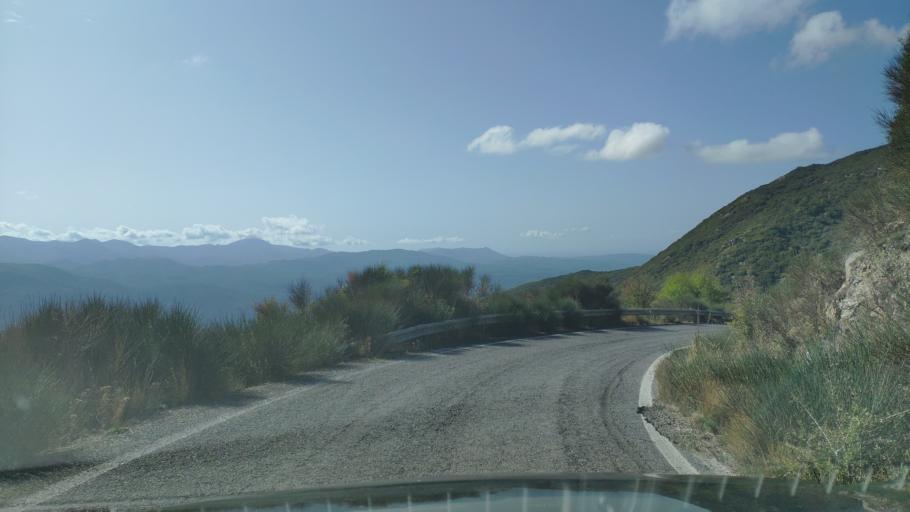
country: GR
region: Peloponnese
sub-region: Nomos Arkadias
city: Dimitsana
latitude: 37.5719
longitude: 22.0188
